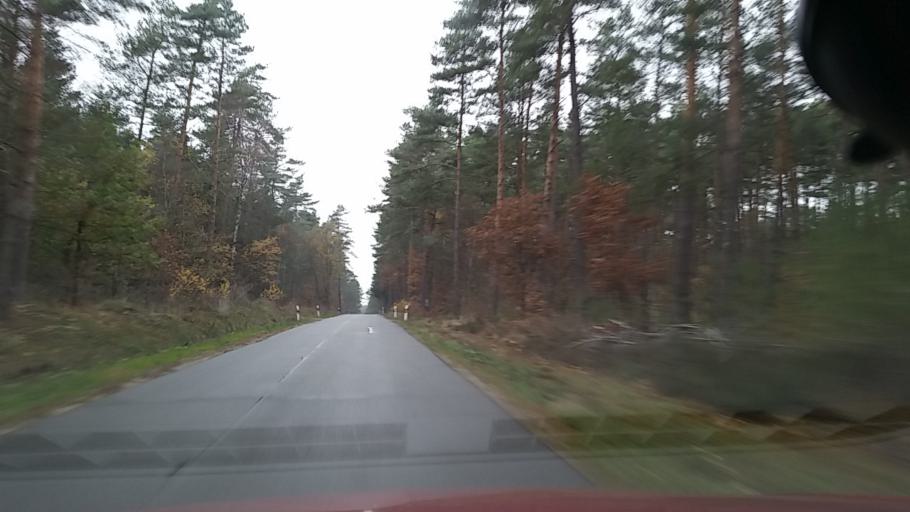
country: DE
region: Lower Saxony
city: Obernholz
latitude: 52.7855
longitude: 10.5711
